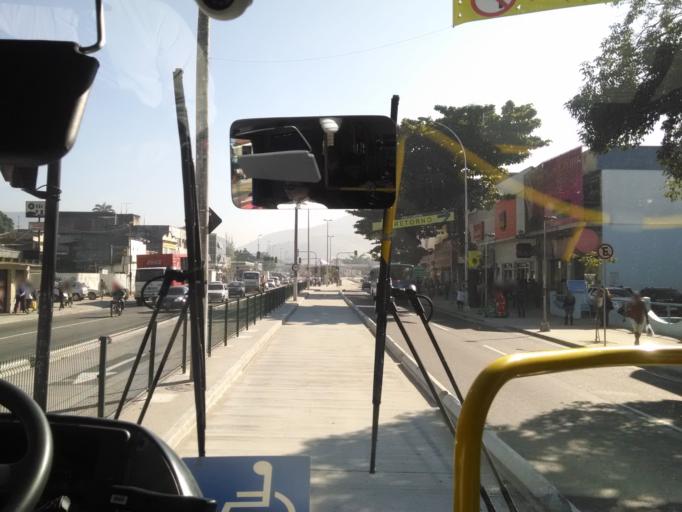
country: BR
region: Rio de Janeiro
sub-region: Sao Joao De Meriti
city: Sao Joao de Meriti
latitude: -22.9263
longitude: -43.3737
